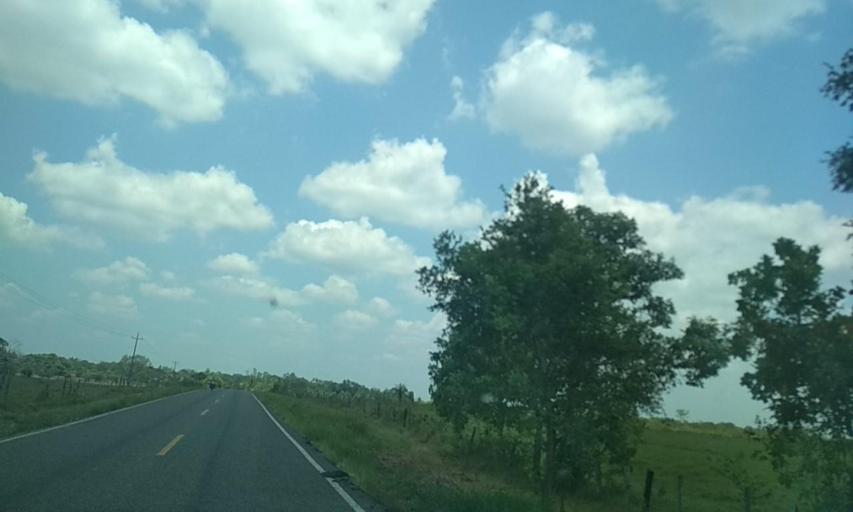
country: MX
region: Tabasco
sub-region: Huimanguillo
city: Huapacal 1ra. Seccion
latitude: 17.7531
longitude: -93.7366
